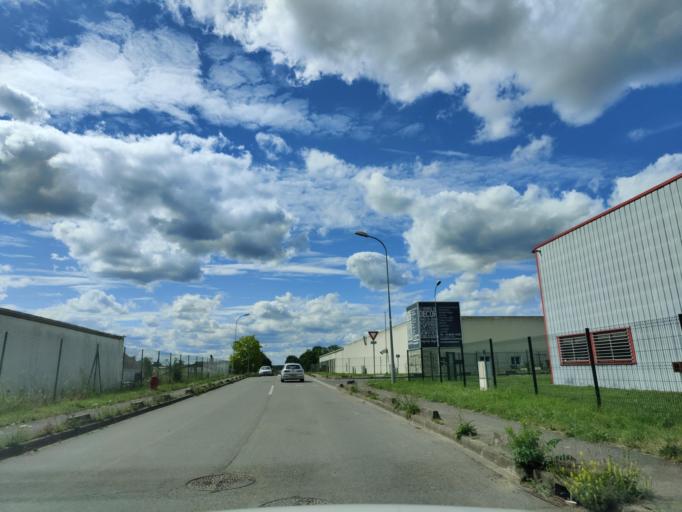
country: FR
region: Ile-de-France
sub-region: Departement de l'Essonne
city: Egly
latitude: 48.5740
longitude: 2.2054
